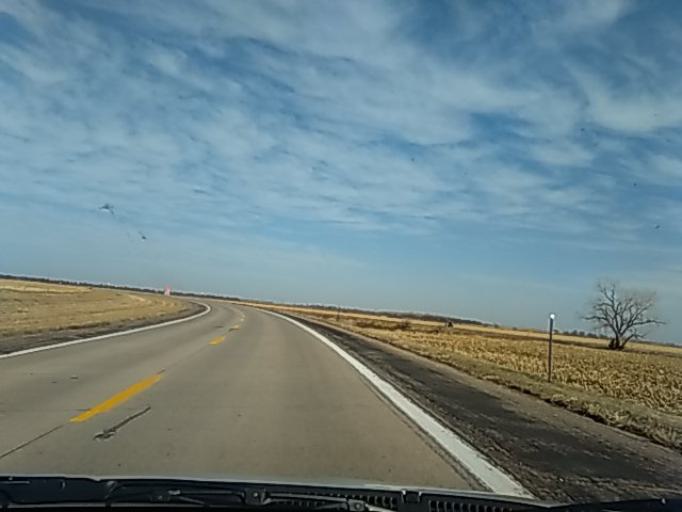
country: US
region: Nebraska
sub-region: Nuckolls County
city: Nelson
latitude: 40.3537
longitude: -98.0536
